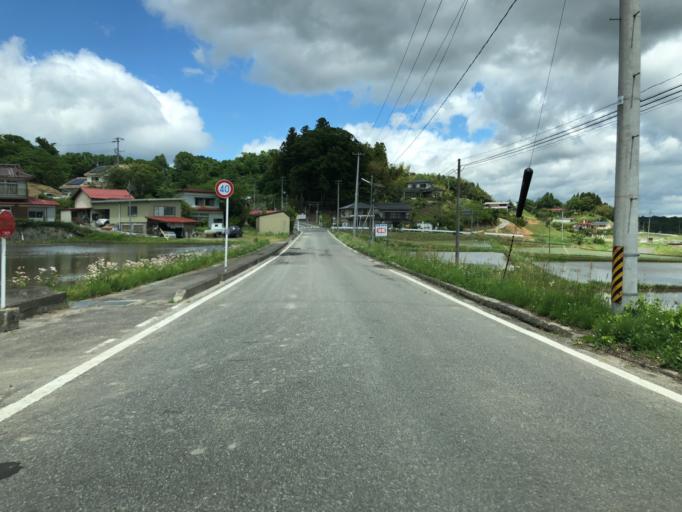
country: JP
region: Fukushima
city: Nihommatsu
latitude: 37.5517
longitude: 140.4687
